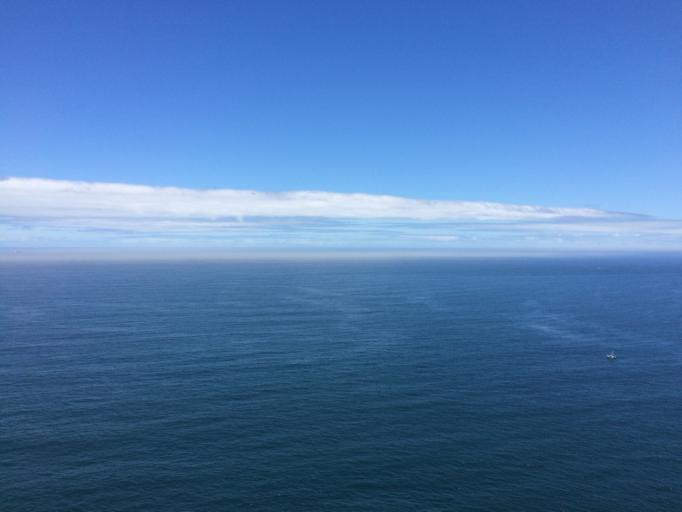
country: ZA
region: Western Cape
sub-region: City of Cape Town
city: Constantia
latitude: -34.0776
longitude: 18.3565
